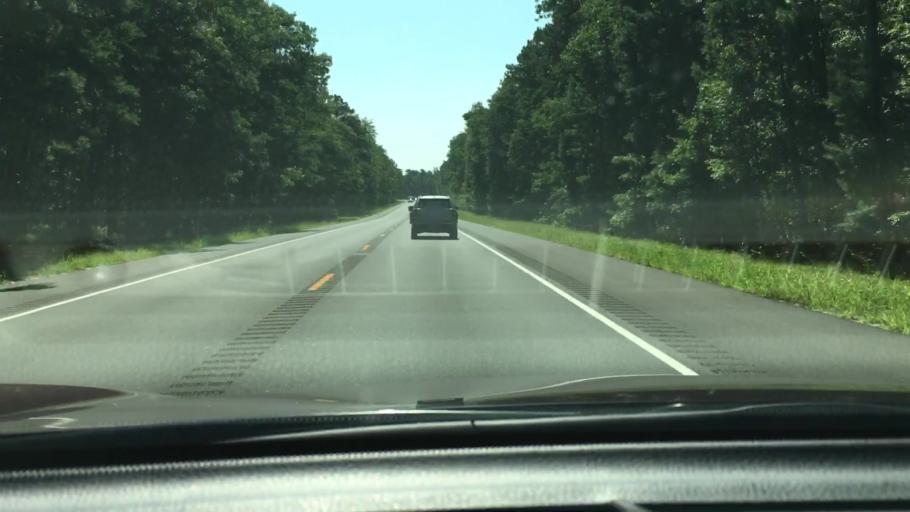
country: US
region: New Jersey
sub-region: Cape May County
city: Woodbine
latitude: 39.3279
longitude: -74.8713
